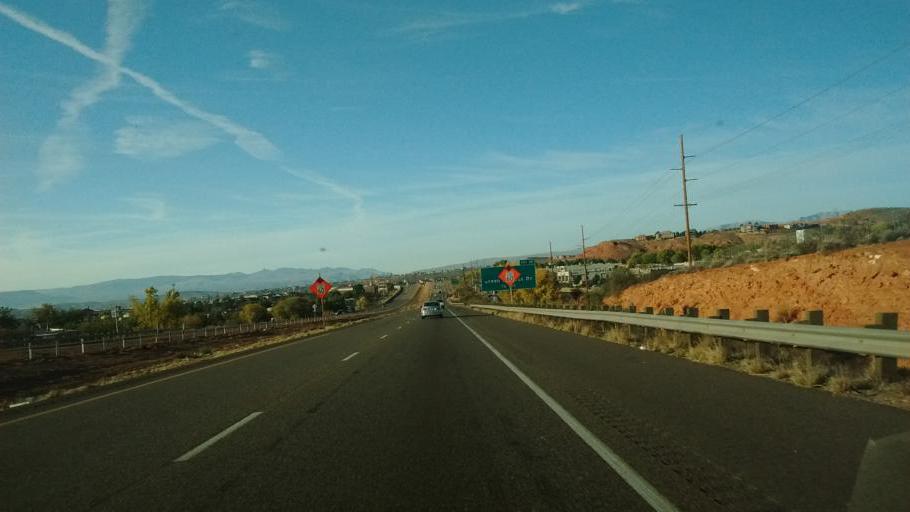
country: US
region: Utah
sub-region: Washington County
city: Washington
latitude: 37.1365
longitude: -113.5138
